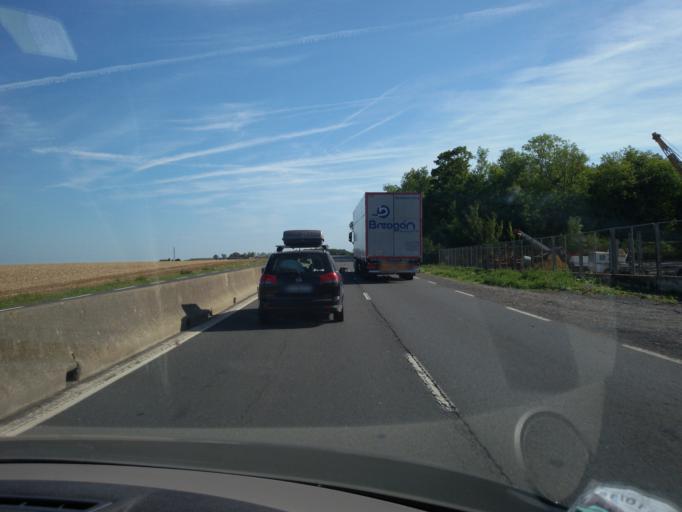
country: FR
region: Ile-de-France
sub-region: Departement de l'Essonne
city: Saclas
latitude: 48.3928
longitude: 2.1117
